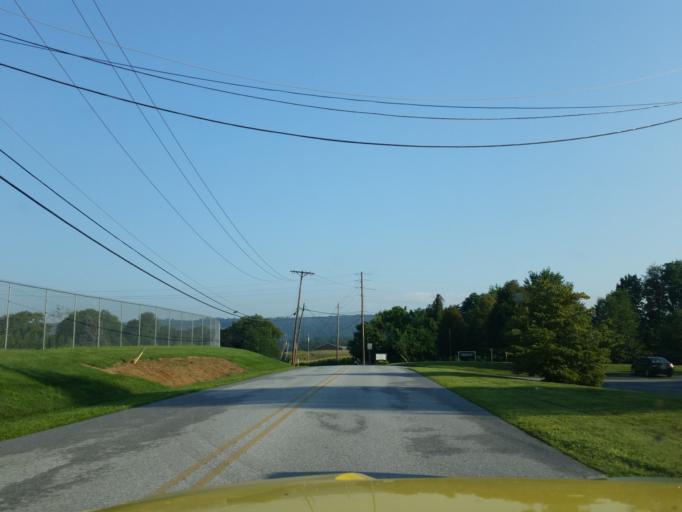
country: US
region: Pennsylvania
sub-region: York County
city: Stonybrook
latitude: 39.9904
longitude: -76.6266
